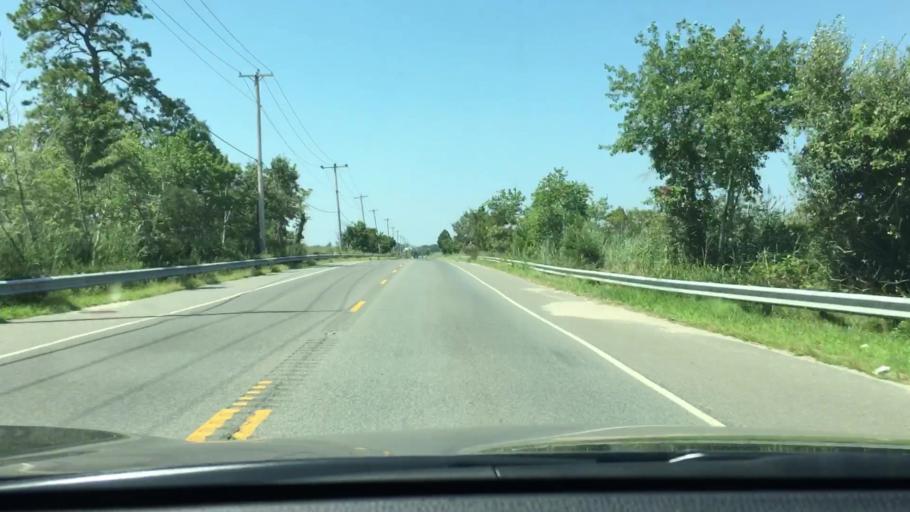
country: US
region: New Jersey
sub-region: Cumberland County
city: Port Norris
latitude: 39.2891
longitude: -74.9733
